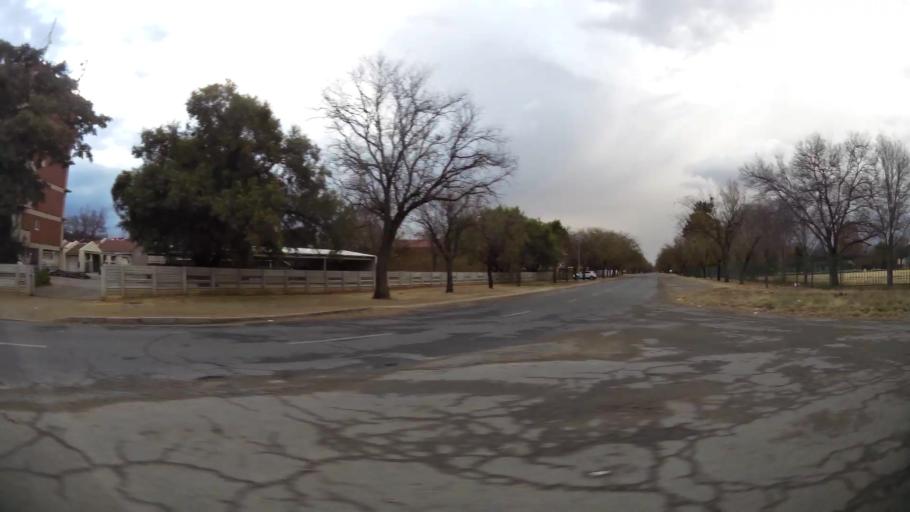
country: ZA
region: Orange Free State
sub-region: Lejweleputswa District Municipality
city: Welkom
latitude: -27.9622
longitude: 26.7397
